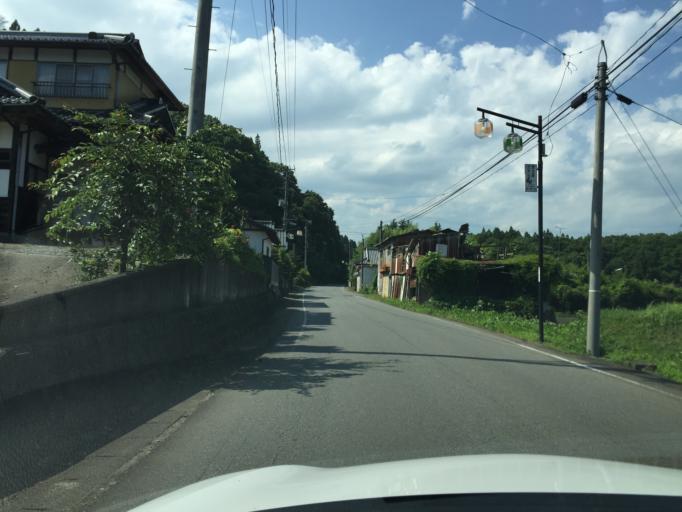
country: JP
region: Ibaraki
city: Kitaibaraki
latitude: 36.9695
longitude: 140.7047
